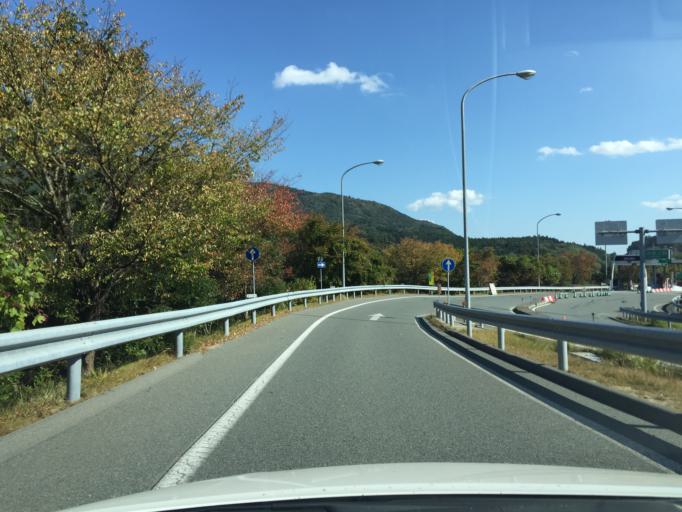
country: JP
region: Fukushima
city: Iwaki
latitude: 37.1024
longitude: 140.7702
